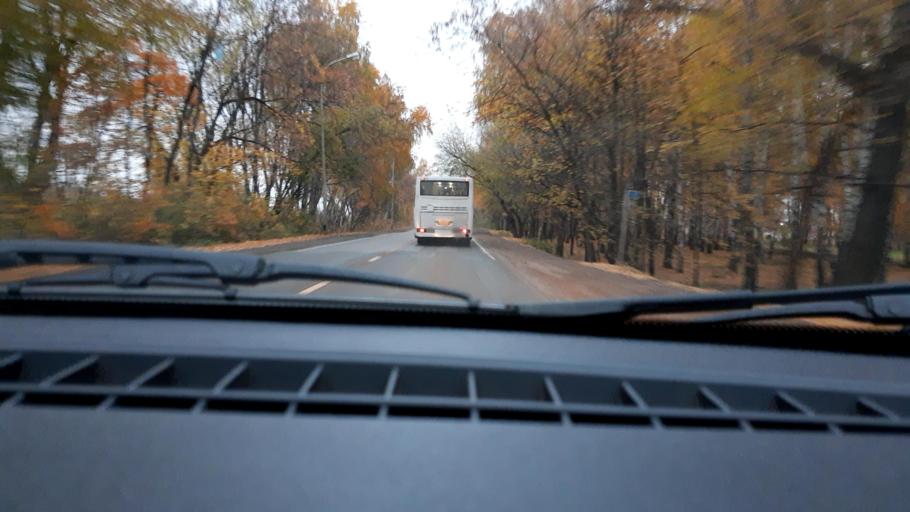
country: RU
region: Bashkortostan
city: Avdon
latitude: 54.7186
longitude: 55.8087
